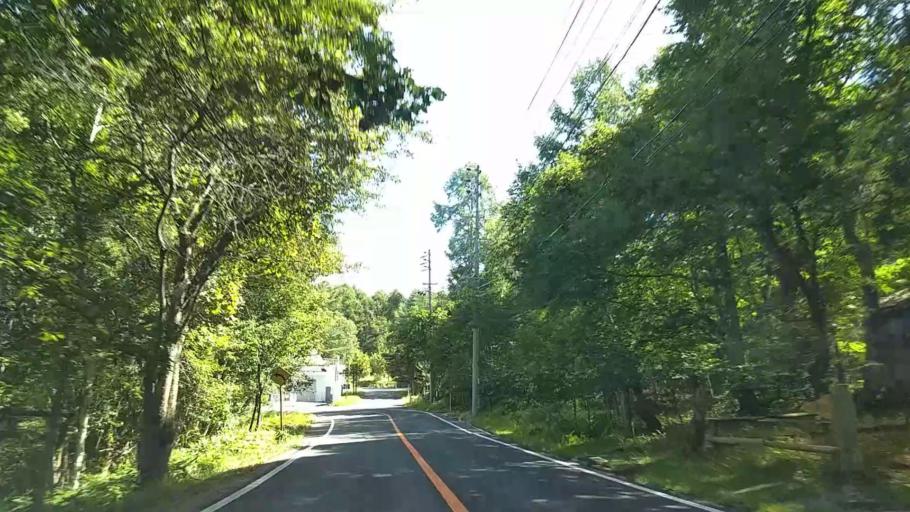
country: JP
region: Nagano
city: Chino
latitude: 36.0615
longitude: 138.2853
